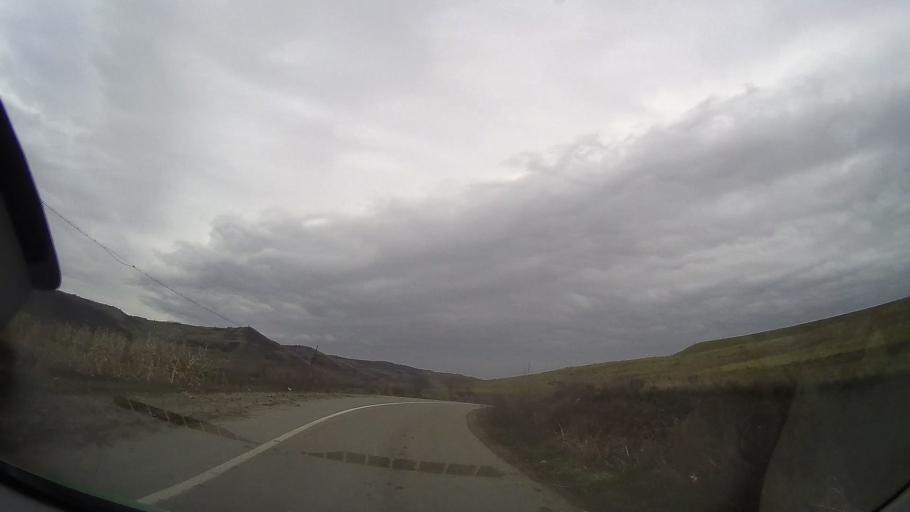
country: RO
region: Mures
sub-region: Comuna Craesti
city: Craiesti
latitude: 46.7850
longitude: 24.4251
